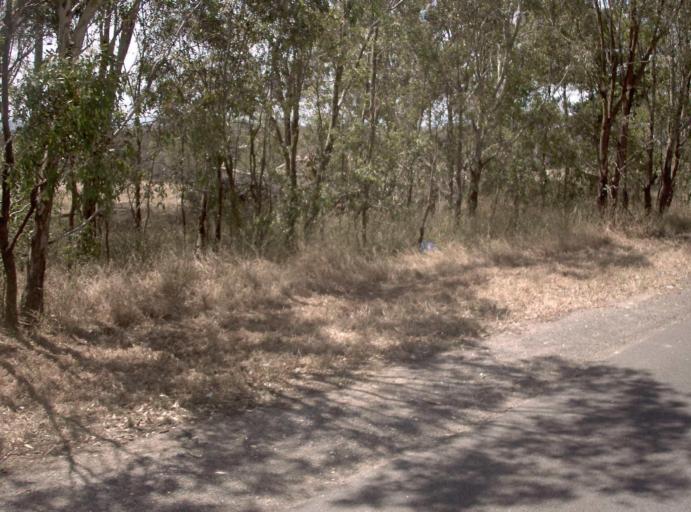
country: AU
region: Victoria
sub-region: Latrobe
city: Traralgon
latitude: -38.1657
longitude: 146.7001
